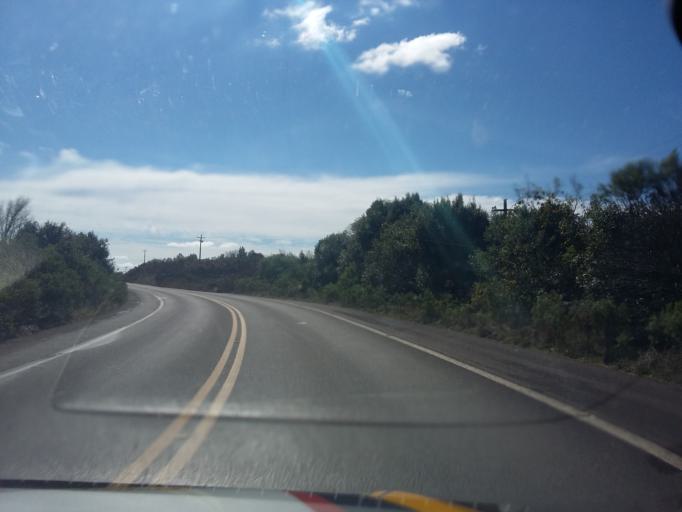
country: BR
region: Rio Grande do Sul
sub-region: Sao Marcos
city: Sao Marcos
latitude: -28.7662
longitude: -51.0913
